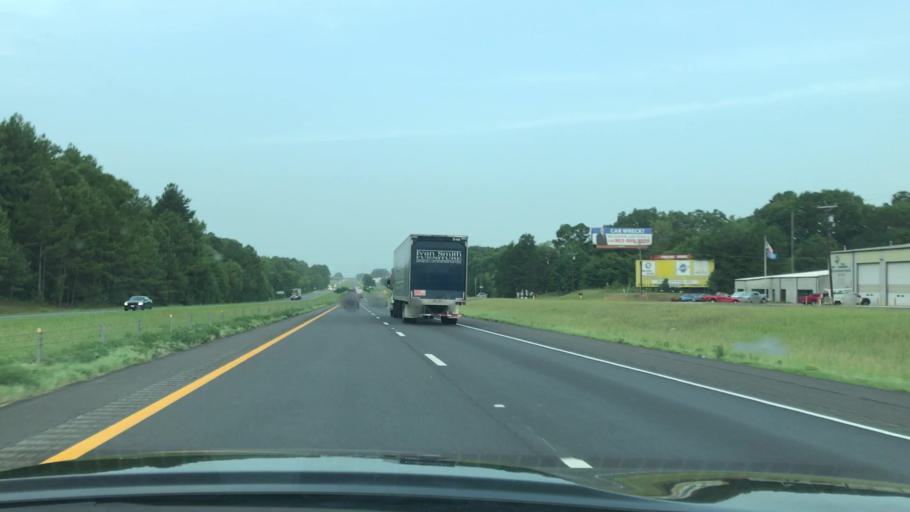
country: US
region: Texas
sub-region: Harrison County
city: Hallsville
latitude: 32.4633
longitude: -94.6455
